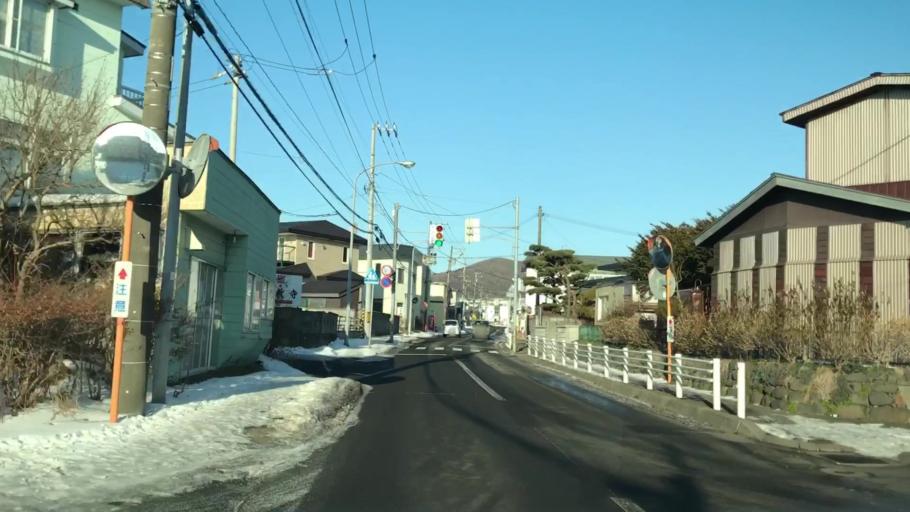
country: JP
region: Hokkaido
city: Muroran
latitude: 42.3641
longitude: 141.0442
